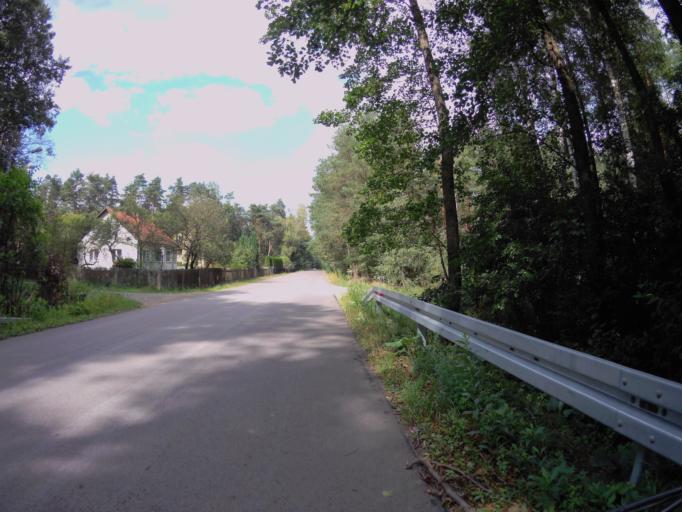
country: PL
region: Subcarpathian Voivodeship
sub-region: Powiat lezajski
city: Brzoza Krolewska
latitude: 50.2748
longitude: 22.3527
